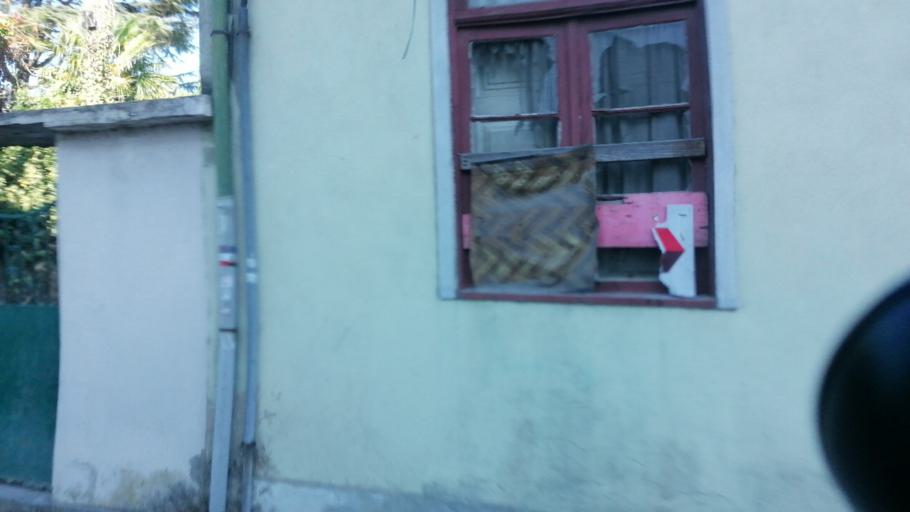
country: PT
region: Porto
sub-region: Santo Tirso
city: Santo Tirso
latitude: 41.3468
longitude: -8.4794
